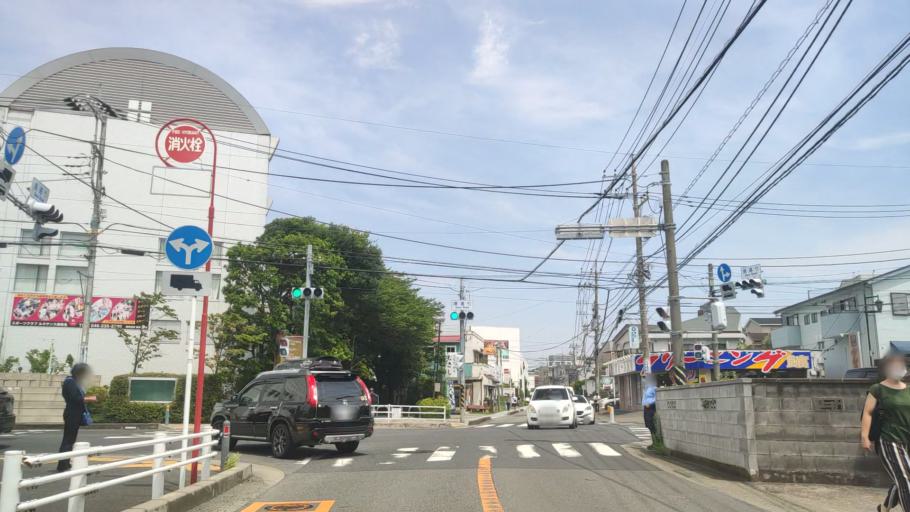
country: JP
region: Kanagawa
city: Atsugi
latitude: 35.4491
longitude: 139.3959
